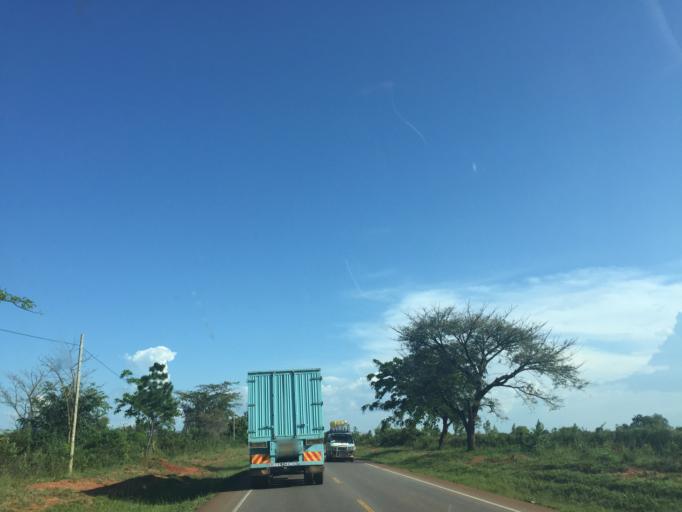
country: UG
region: Central Region
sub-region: Nakasongola District
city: Nakasongola
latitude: 1.2934
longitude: 32.4257
